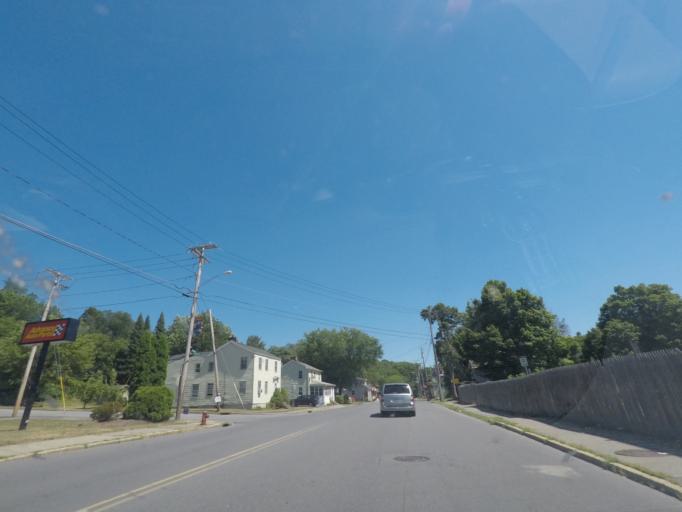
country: US
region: New York
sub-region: Rensselaer County
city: Wynantskill
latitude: 42.7012
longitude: -73.6546
